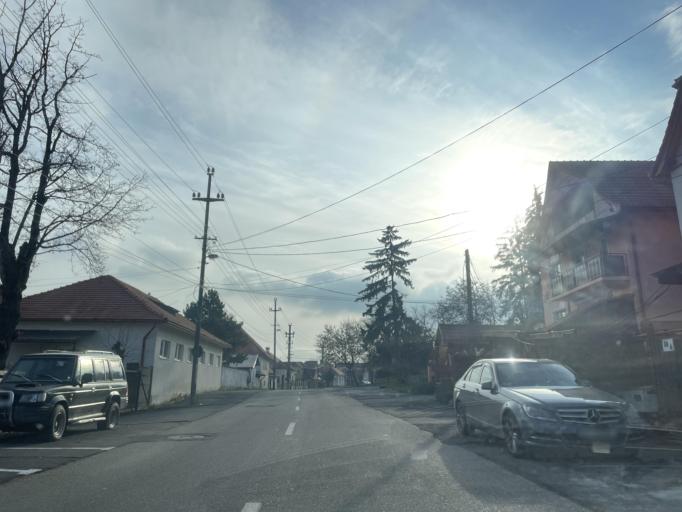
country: RO
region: Mures
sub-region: Municipiul Reghin
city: Reghin
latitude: 46.7831
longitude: 24.6945
